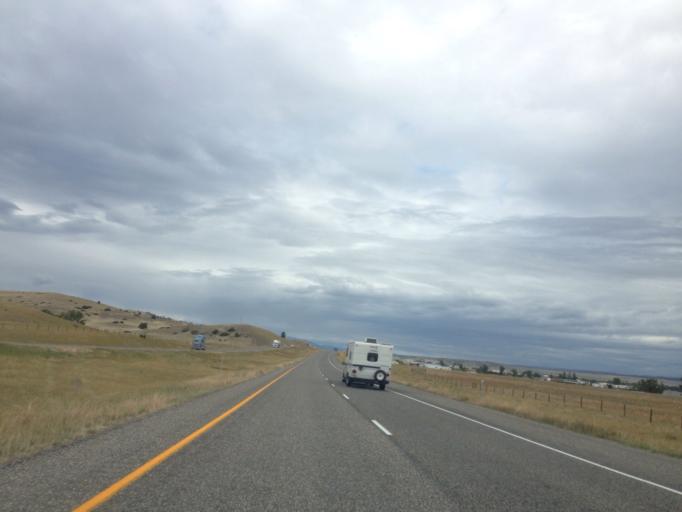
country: US
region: Montana
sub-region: Sweet Grass County
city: Big Timber
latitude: 45.7457
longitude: -109.7713
